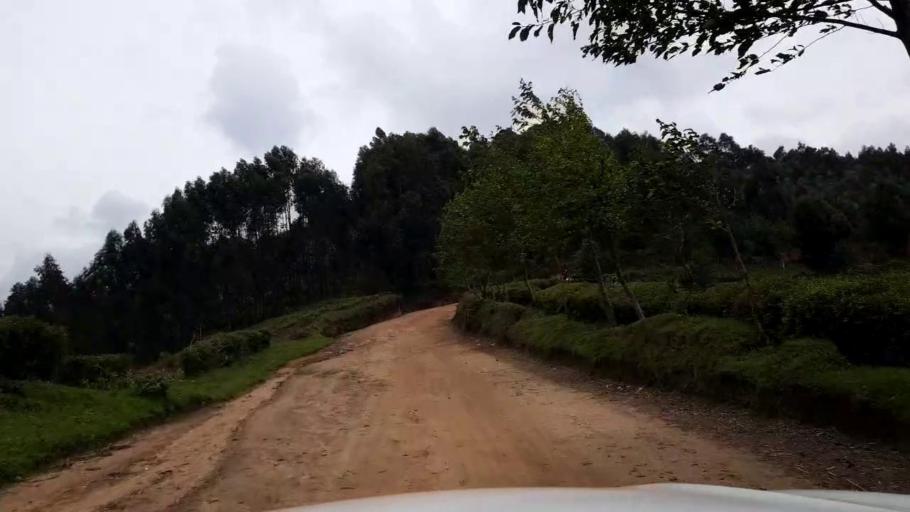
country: RW
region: Western Province
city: Kibuye
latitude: -1.9520
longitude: 29.4084
